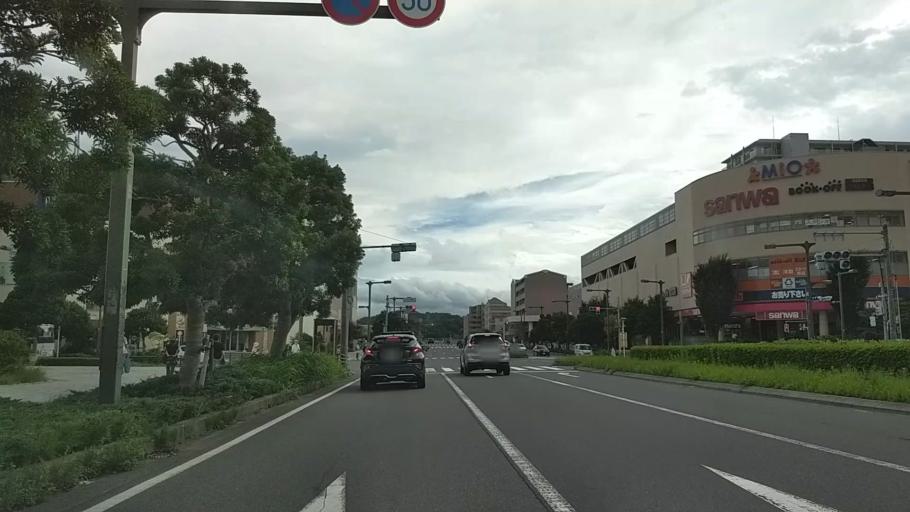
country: JP
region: Tokyo
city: Hachioji
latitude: 35.6322
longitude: 139.3292
